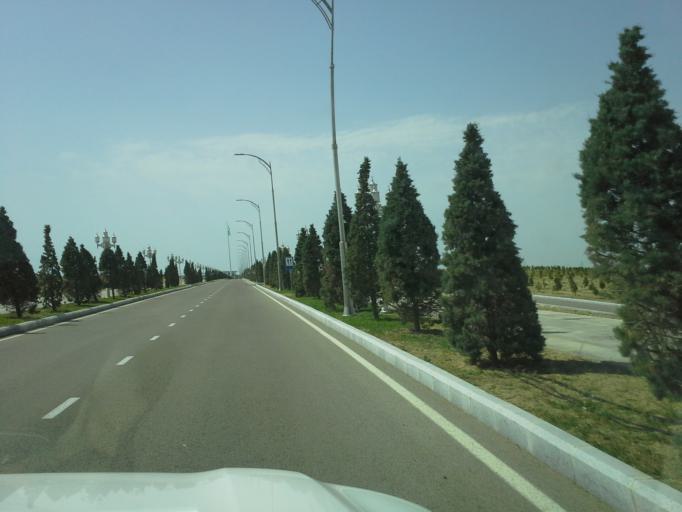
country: TM
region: Balkan
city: Turkmenbasy
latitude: 39.9517
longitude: 52.8744
